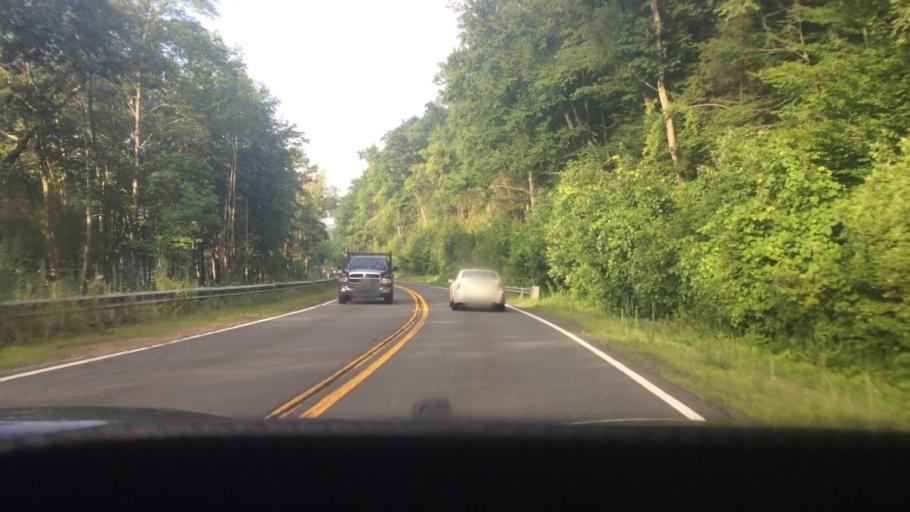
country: US
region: Massachusetts
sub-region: Franklin County
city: Erving
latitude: 42.6068
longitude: -72.4288
